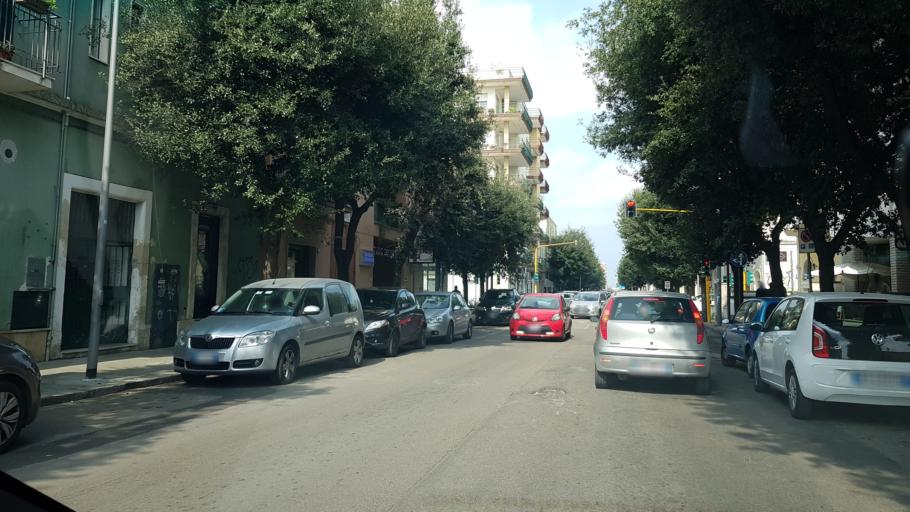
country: IT
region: Apulia
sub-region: Provincia di Lecce
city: Castromediano
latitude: 40.3388
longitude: 18.1771
